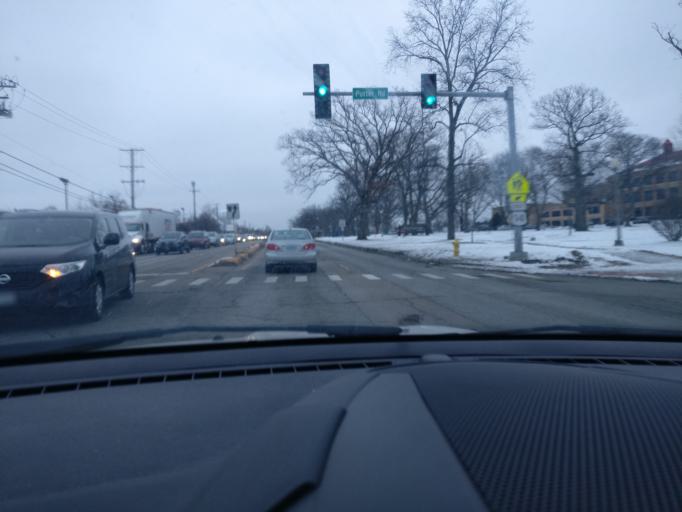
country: US
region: Illinois
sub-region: Cook County
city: Des Plaines
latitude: 42.0393
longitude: -87.8600
